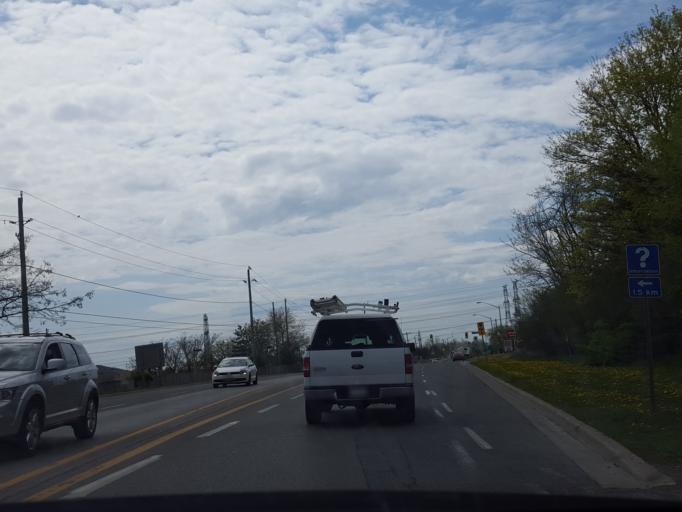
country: CA
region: Ontario
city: Oshawa
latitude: 43.8992
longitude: -78.6916
